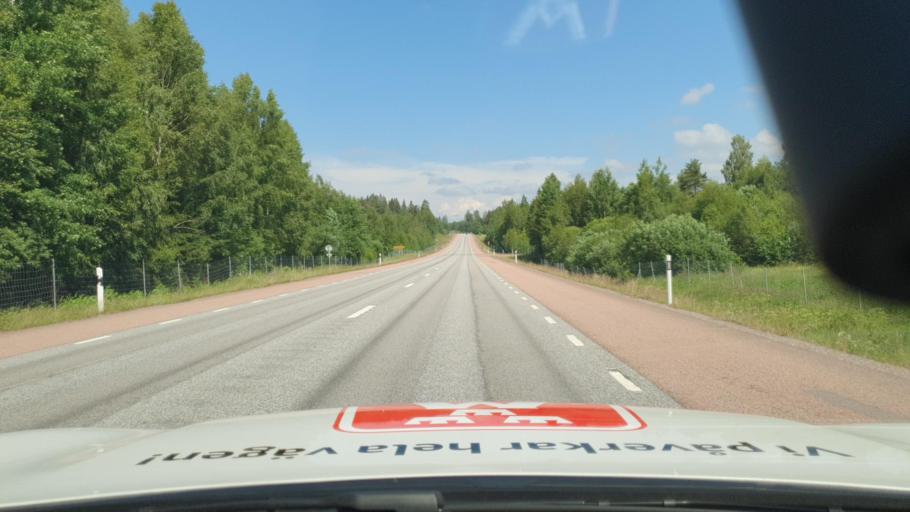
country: SE
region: Vaermland
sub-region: Torsby Kommun
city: Torsby
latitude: 60.1867
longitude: 13.0172
